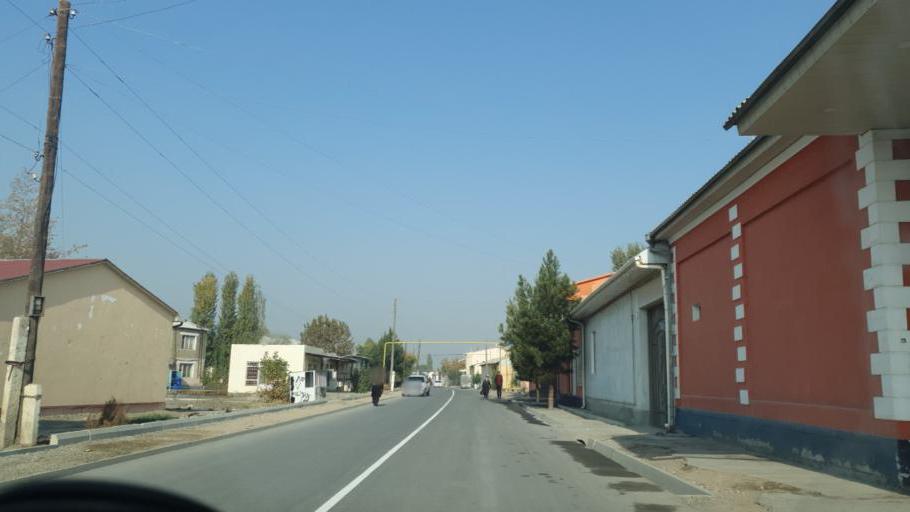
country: UZ
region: Fergana
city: Qo`qon
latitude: 40.5817
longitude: 70.9114
